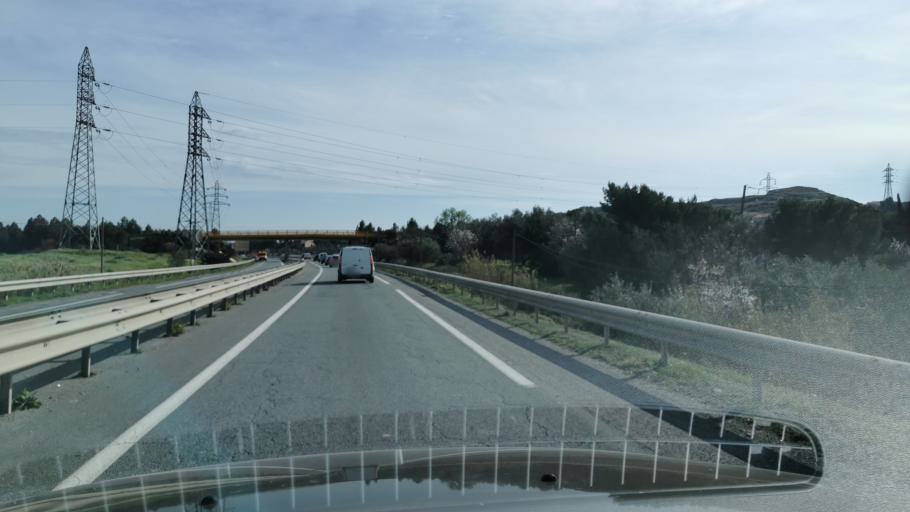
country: FR
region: Languedoc-Roussillon
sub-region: Departement de l'Aude
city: Narbonne
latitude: 43.1729
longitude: 2.9759
